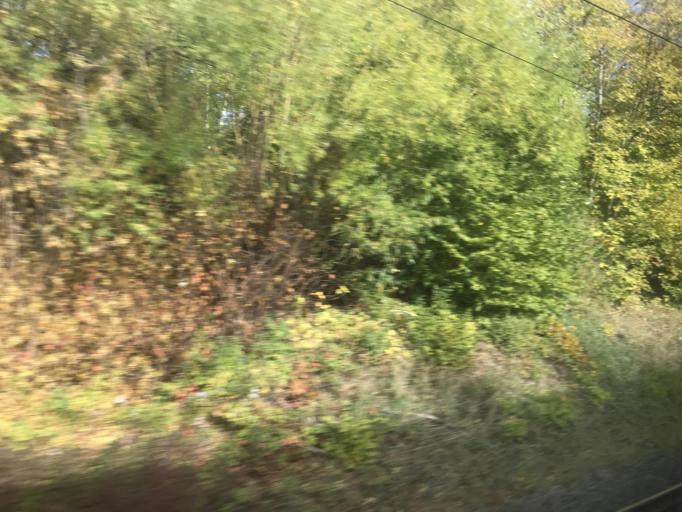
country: DE
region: North Rhine-Westphalia
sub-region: Regierungsbezirk Arnsberg
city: Dortmund
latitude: 51.5420
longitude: 7.4905
